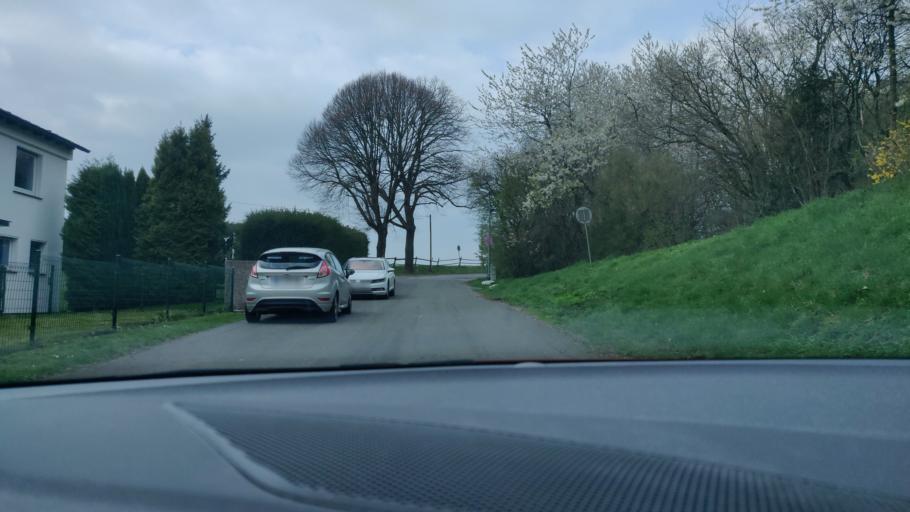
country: DE
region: North Rhine-Westphalia
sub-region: Regierungsbezirk Dusseldorf
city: Velbert
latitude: 51.3235
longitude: 7.0435
